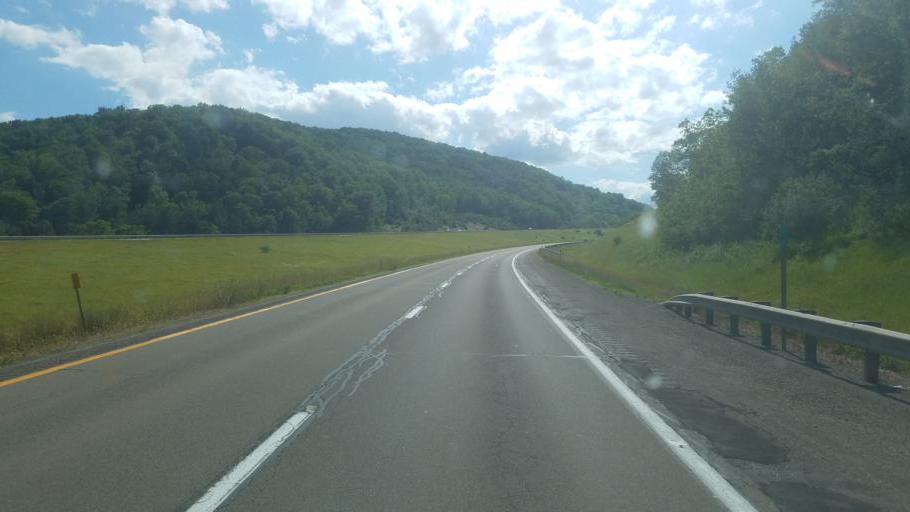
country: US
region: New York
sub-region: Allegany County
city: Alfred
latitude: 42.3158
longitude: -77.7542
